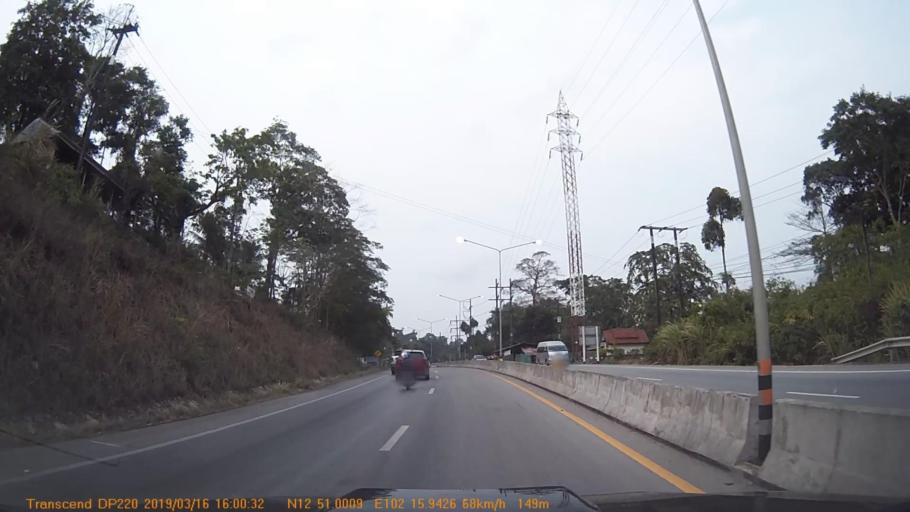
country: TH
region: Chanthaburi
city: Pong Nam Ron
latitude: 12.8502
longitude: 102.2658
